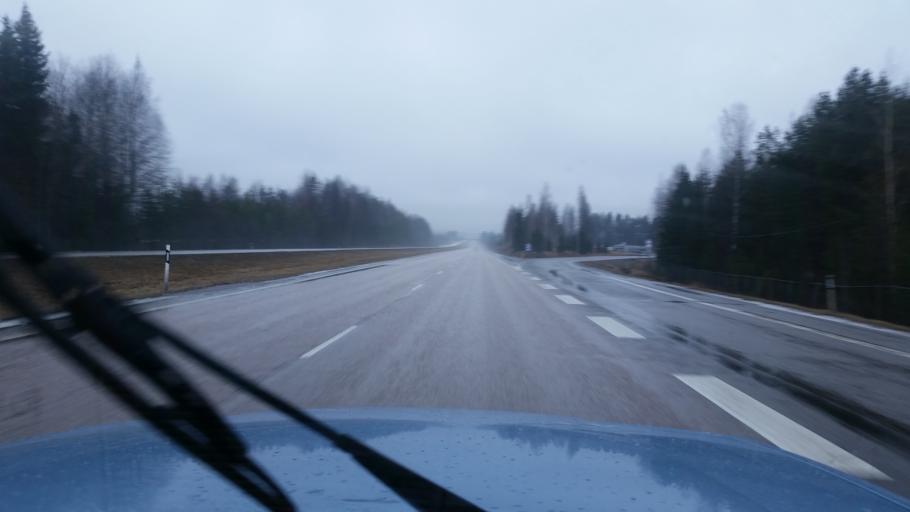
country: FI
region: Uusimaa
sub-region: Helsinki
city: Nurmijaervi
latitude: 60.5033
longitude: 24.8506
